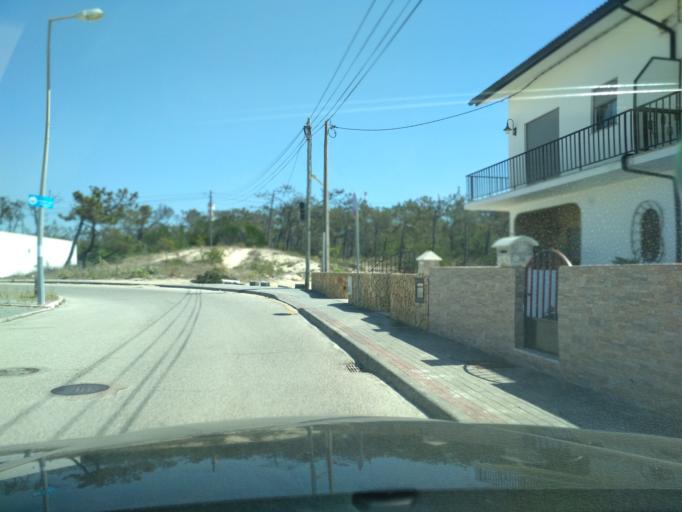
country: PT
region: Coimbra
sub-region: Figueira da Foz
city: Lavos
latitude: 40.0545
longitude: -8.8857
